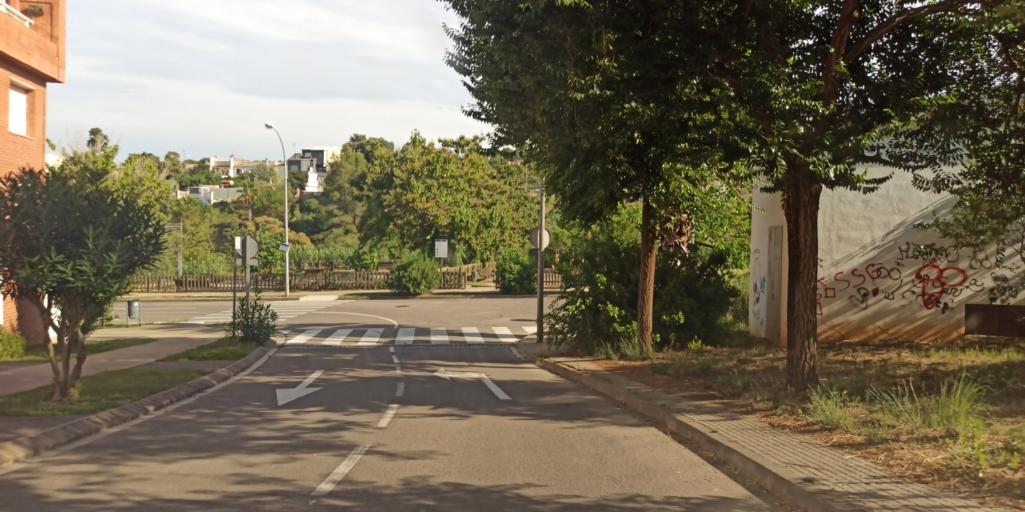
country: ES
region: Catalonia
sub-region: Provincia de Barcelona
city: Sant Boi de Llobregat
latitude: 41.3478
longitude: 2.0203
